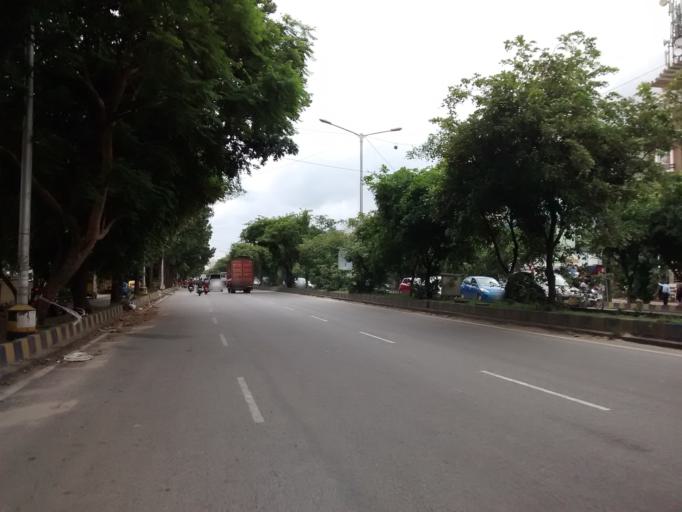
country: IN
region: Karnataka
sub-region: Bangalore Urban
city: Bangalore
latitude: 13.0309
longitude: 77.6305
